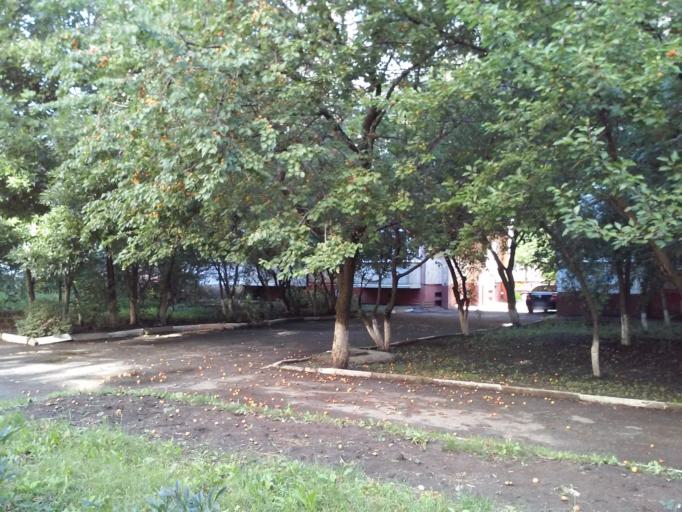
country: RU
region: Belgorod
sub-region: Belgorodskiy Rayon
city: Belgorod
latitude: 50.5594
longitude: 36.5695
